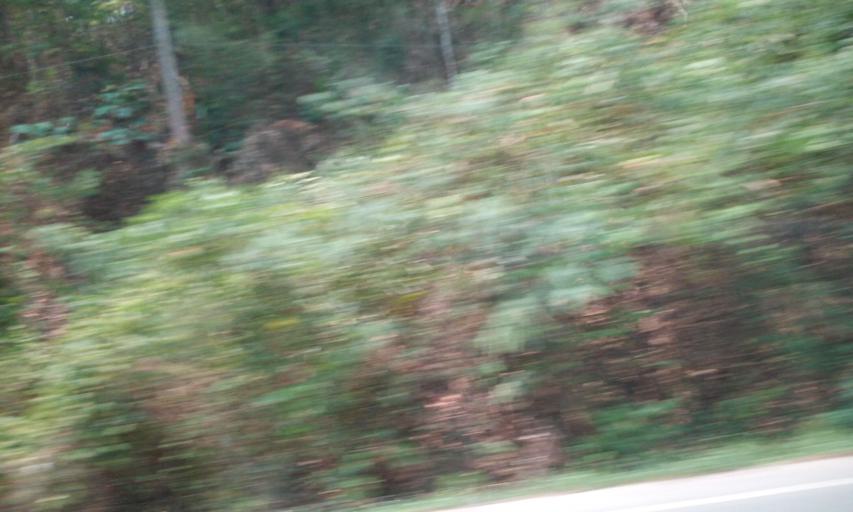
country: TH
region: Chiang Rai
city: Pa Daet
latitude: 19.6147
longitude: 100.0079
